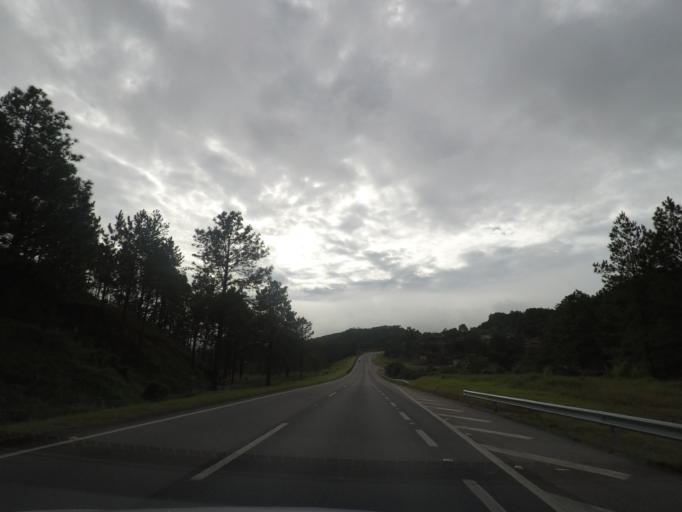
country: BR
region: Parana
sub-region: Campina Grande Do Sul
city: Campina Grande do Sul
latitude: -25.1091
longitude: -48.8376
